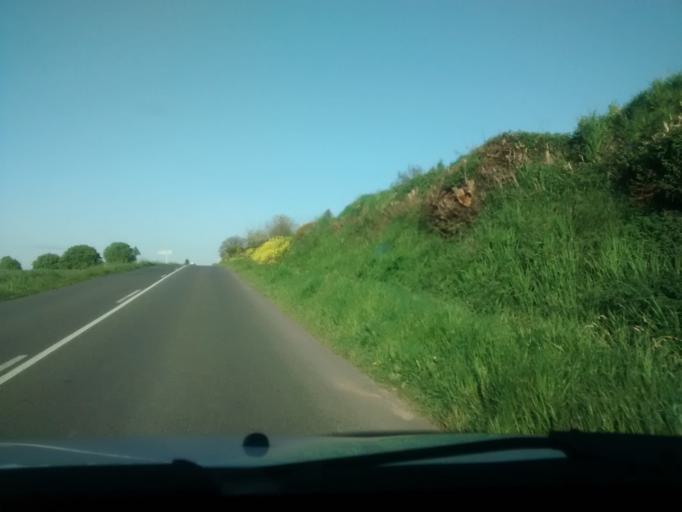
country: FR
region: Brittany
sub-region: Departement d'Ille-et-Vilaine
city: Pleine-Fougeres
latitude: 48.5496
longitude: -1.5804
